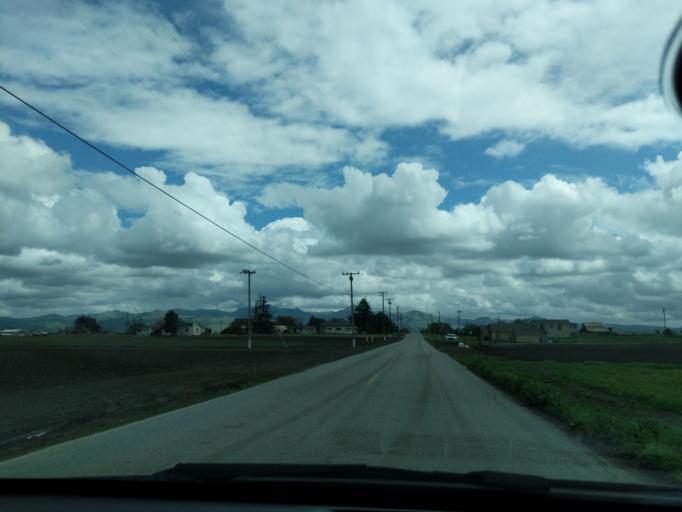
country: US
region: California
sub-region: San Benito County
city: Hollister
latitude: 36.8704
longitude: -121.4254
